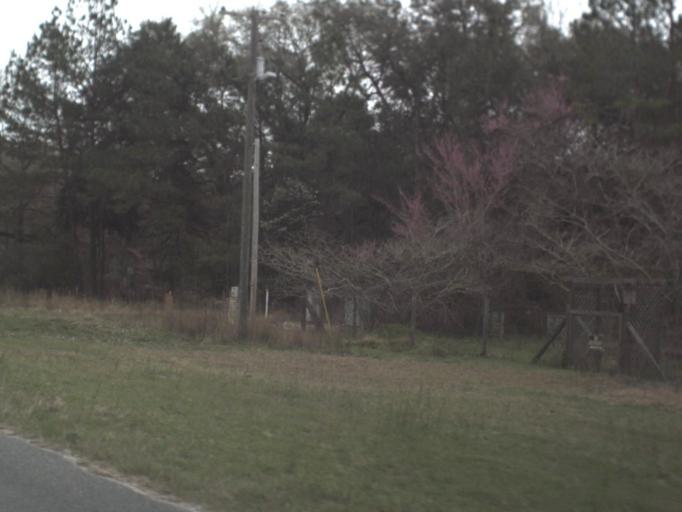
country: US
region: Florida
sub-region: Wakulla County
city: Crawfordville
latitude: 30.1562
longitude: -84.2578
